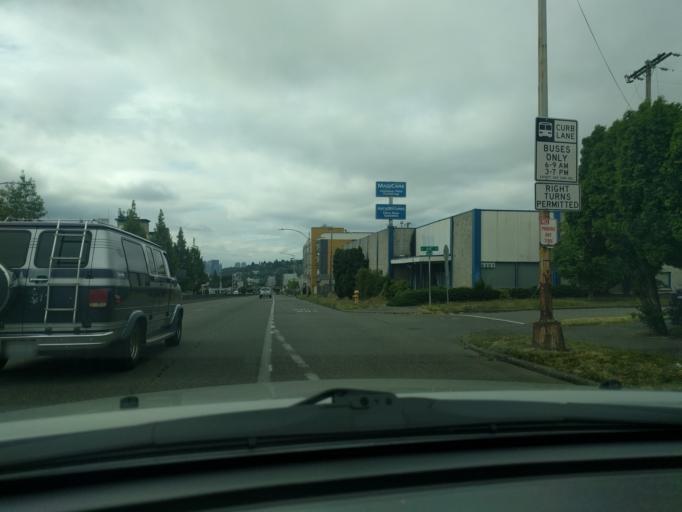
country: US
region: Washington
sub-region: King County
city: Seattle
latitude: 47.6603
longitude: -122.3475
